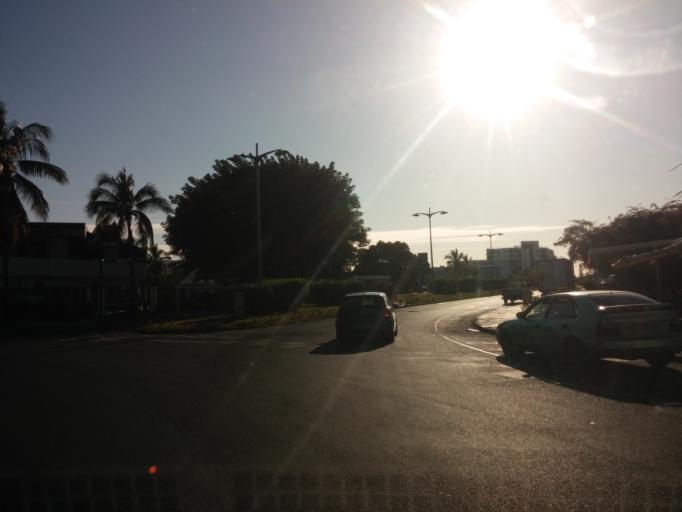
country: RE
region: Reunion
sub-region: Reunion
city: Le Port
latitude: -20.9337
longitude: 55.2921
